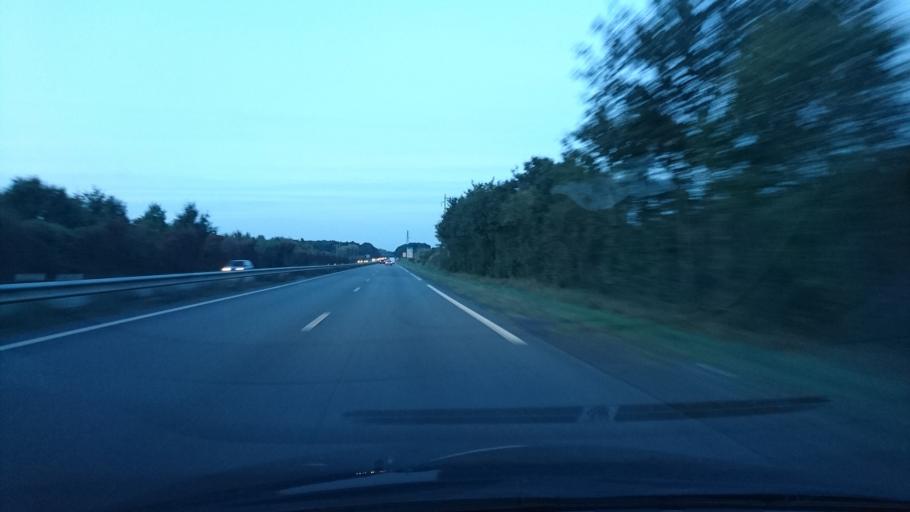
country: FR
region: Brittany
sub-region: Departement d'Ille-et-Vilaine
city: Bruz
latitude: 48.0353
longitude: -1.7583
